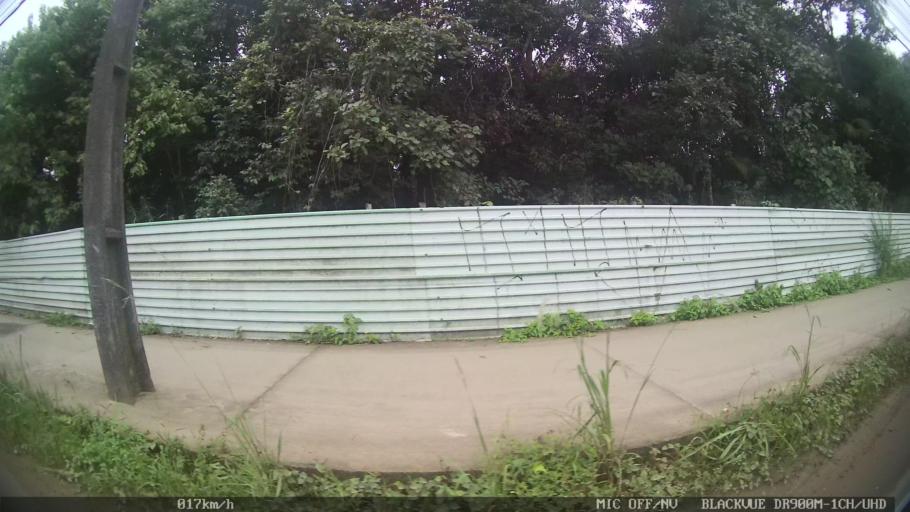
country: BR
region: Santa Catarina
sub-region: Joinville
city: Joinville
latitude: -26.2647
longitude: -48.9244
